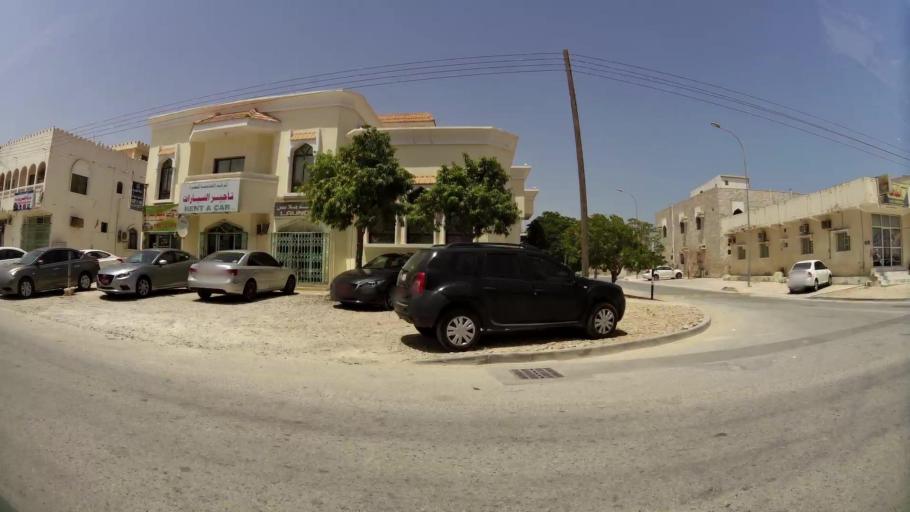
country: OM
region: Zufar
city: Salalah
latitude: 17.0130
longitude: 54.0792
